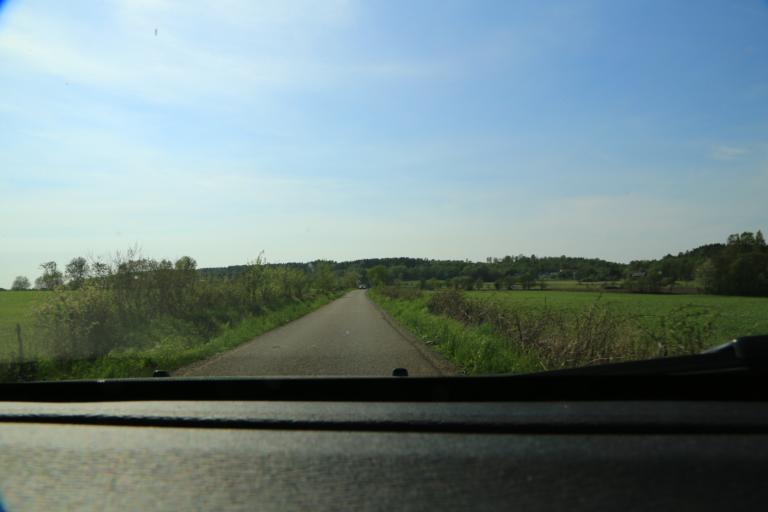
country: SE
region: Halland
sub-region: Varbergs Kommun
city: Varberg
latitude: 57.1762
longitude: 12.2600
